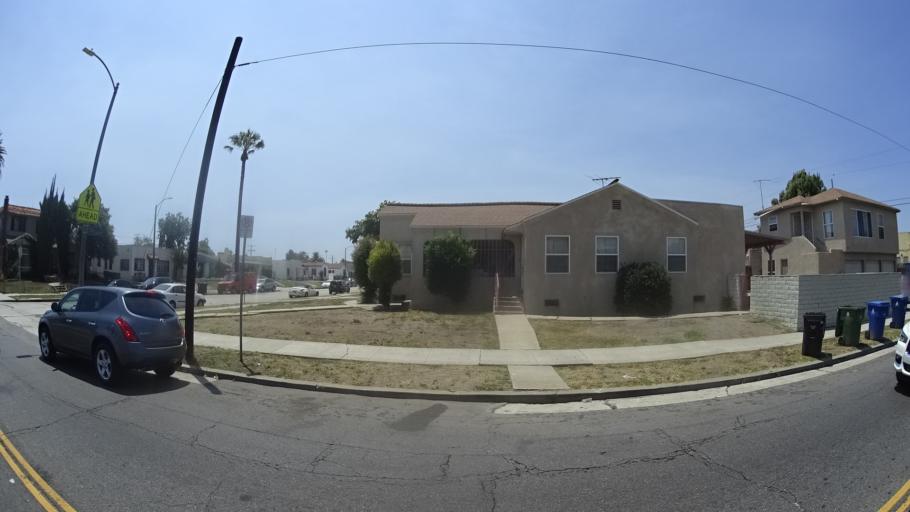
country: US
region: California
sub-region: Los Angeles County
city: Westmont
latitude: 33.9738
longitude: -118.3175
